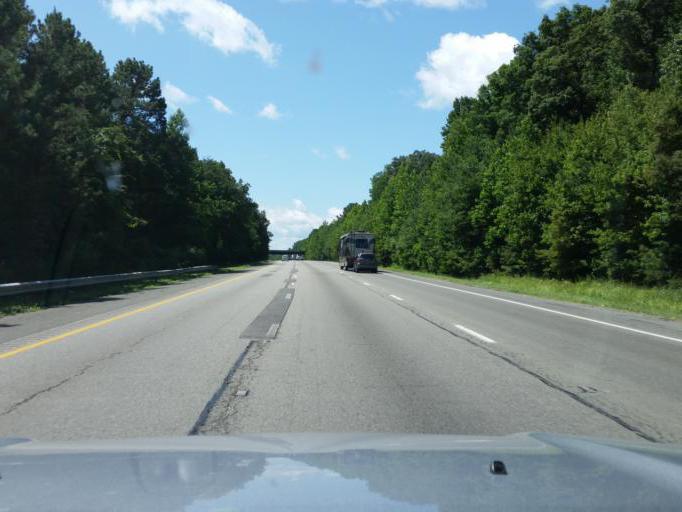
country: US
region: Virginia
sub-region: Hanover County
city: Ashland
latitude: 37.8213
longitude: -77.4575
